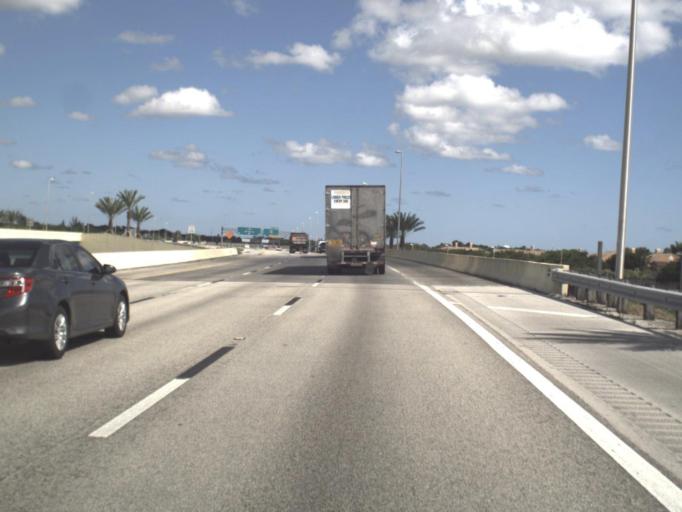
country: US
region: Florida
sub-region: Palm Beach County
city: Boca Pointe
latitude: 26.3007
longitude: -80.1871
